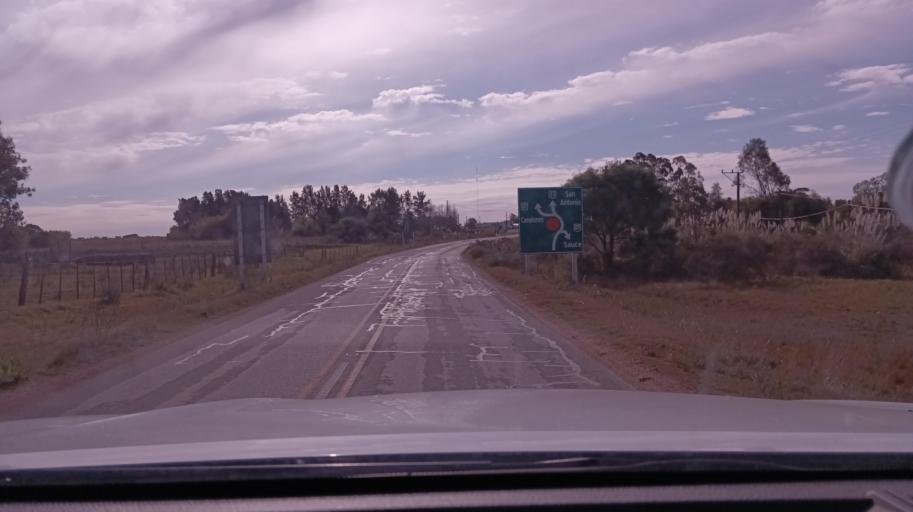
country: UY
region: Canelones
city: Sauce
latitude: -34.6272
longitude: -56.1113
